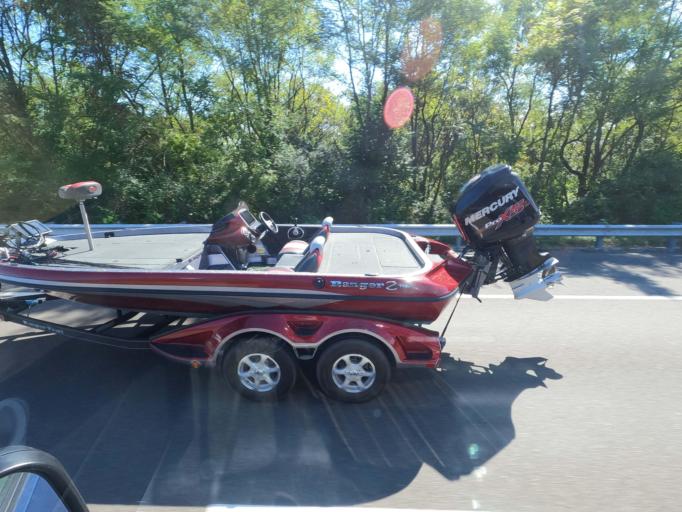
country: US
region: Tennessee
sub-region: Grainger County
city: Bean Station
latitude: 36.3237
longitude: -83.2857
